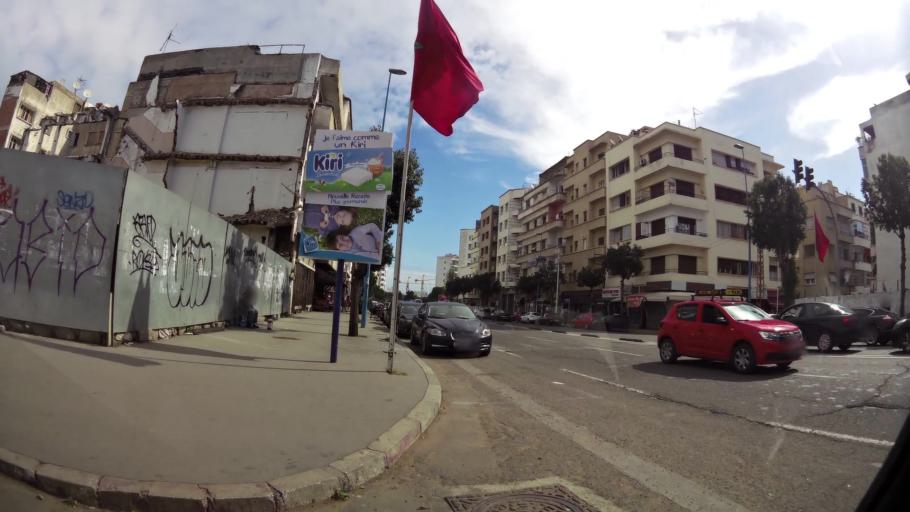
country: MA
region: Grand Casablanca
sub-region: Casablanca
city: Casablanca
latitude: 33.5835
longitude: -7.6320
